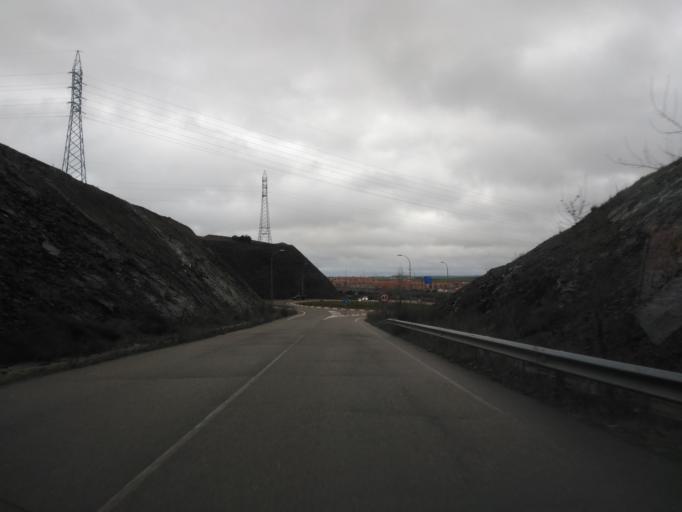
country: ES
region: Castille and Leon
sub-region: Provincia de Salamanca
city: Villamayor
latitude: 40.9641
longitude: -5.7044
